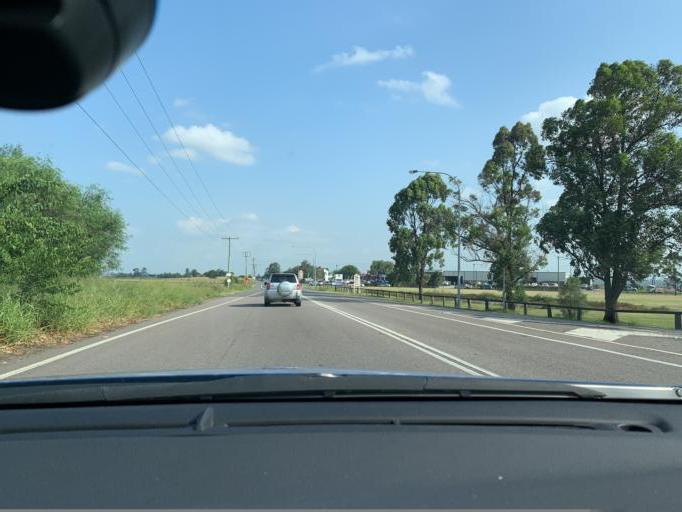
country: AU
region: New South Wales
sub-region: Singleton
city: Singleton
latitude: -32.5750
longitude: 151.1837
